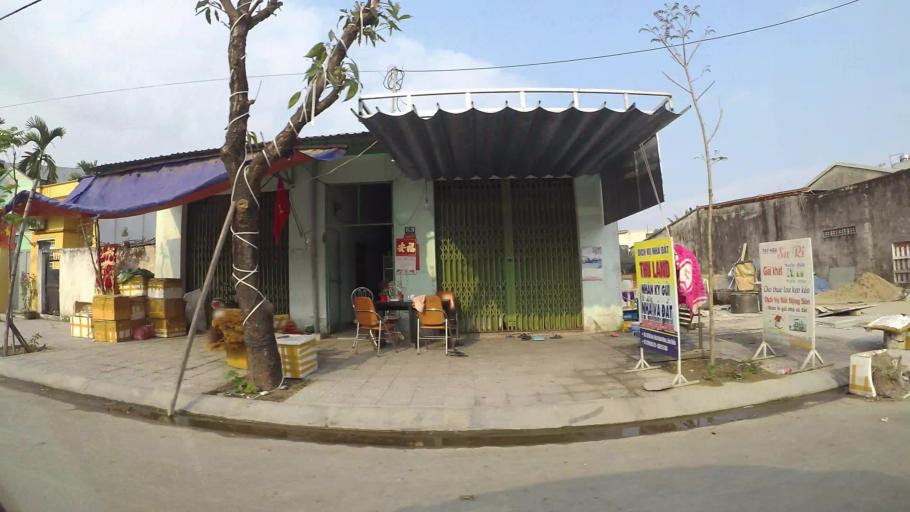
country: VN
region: Da Nang
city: Lien Chieu
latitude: 16.0509
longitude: 108.1547
